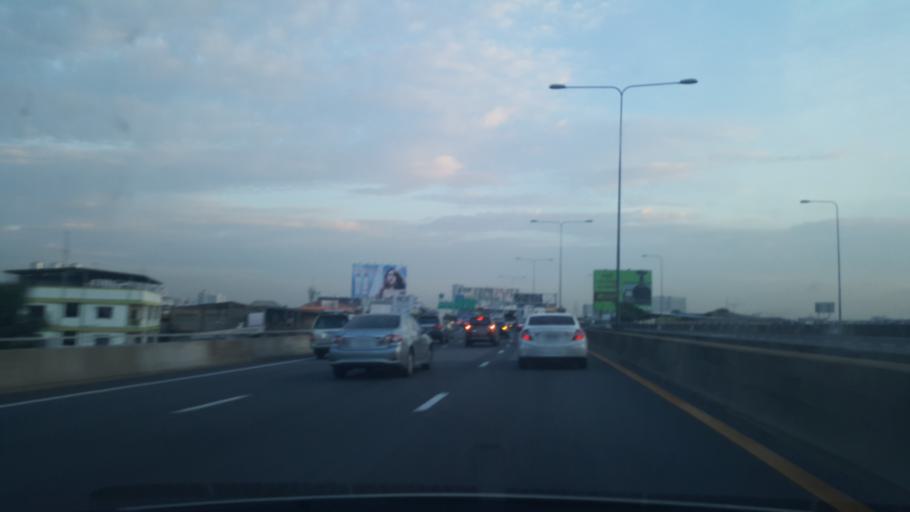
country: TH
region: Bangkok
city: Sathon
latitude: 13.7010
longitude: 100.5194
